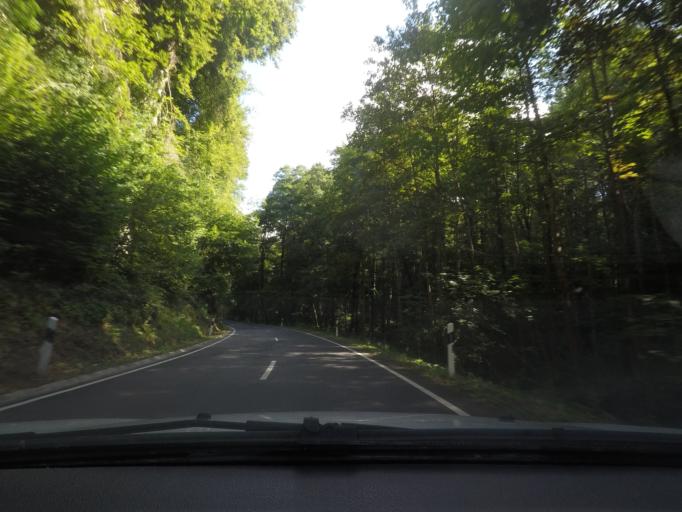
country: LU
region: Grevenmacher
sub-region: Canton d'Echternach
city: Waldbillig
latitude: 49.7758
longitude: 6.2915
